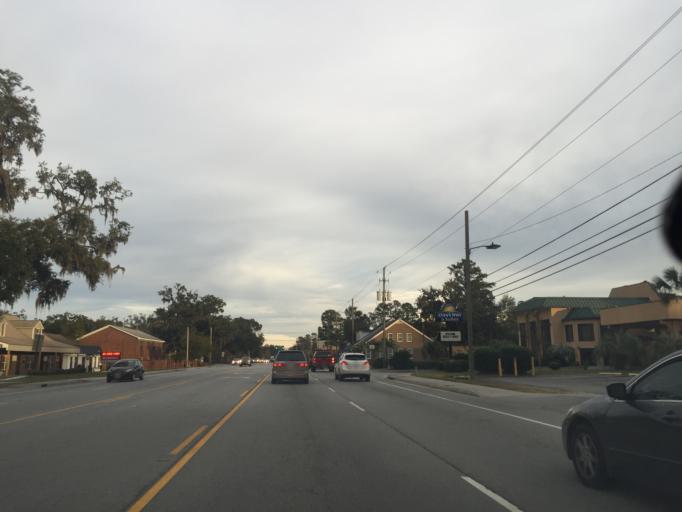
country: US
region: Georgia
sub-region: Chatham County
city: Isle of Hope
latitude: 32.0130
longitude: -81.1105
